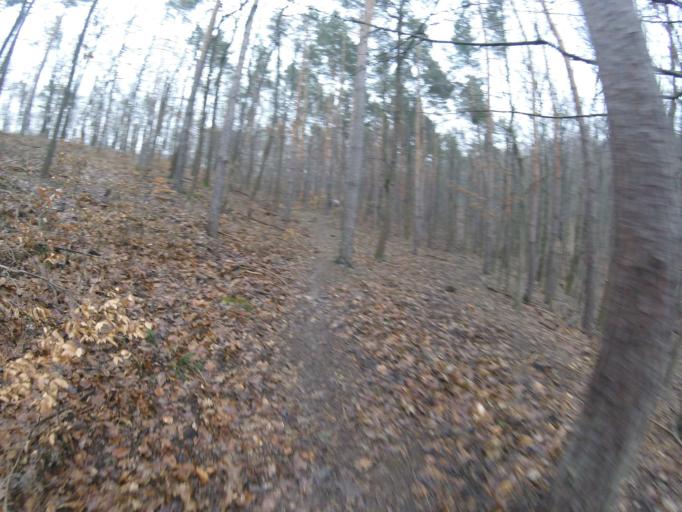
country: HU
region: Pest
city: Visegrad
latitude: 47.7667
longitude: 18.9889
